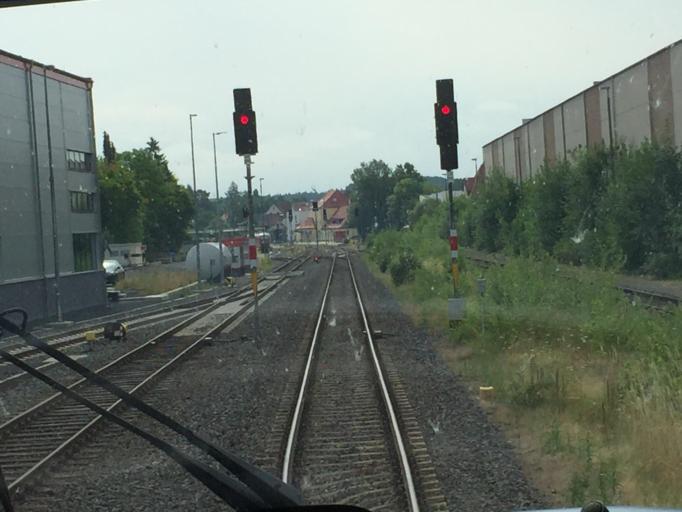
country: DE
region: Hesse
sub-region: Regierungsbezirk Kassel
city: Korbach
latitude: 51.2793
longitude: 8.8719
